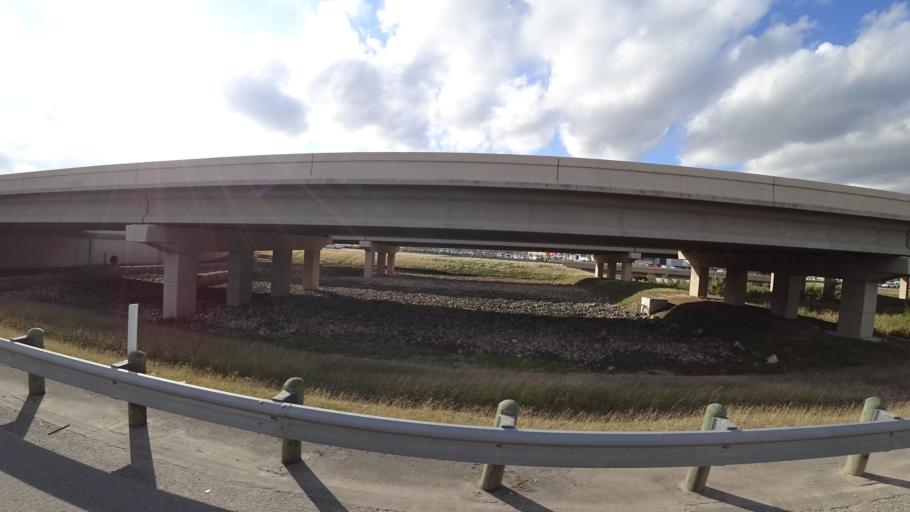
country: US
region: Texas
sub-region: Williamson County
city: Cedar Park
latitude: 30.5349
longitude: -97.8163
